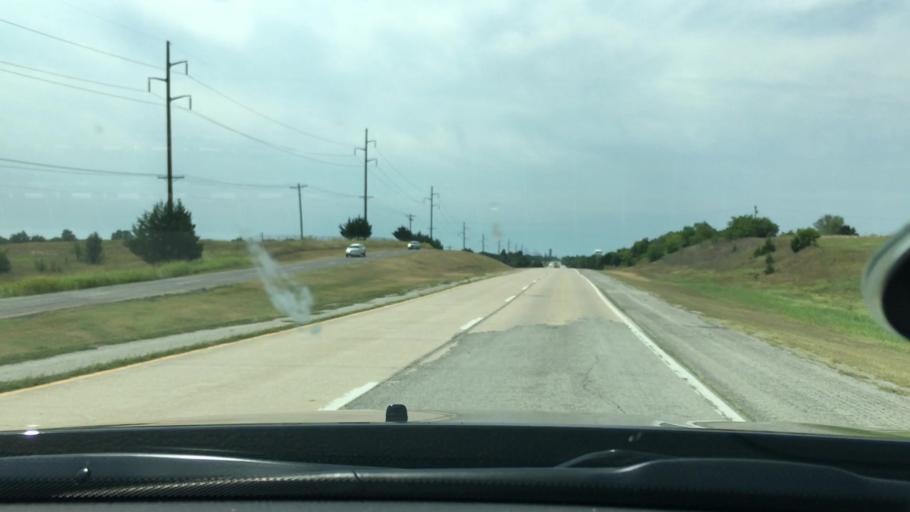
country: US
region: Oklahoma
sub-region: Carter County
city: Ardmore
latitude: 34.2283
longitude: -97.1433
